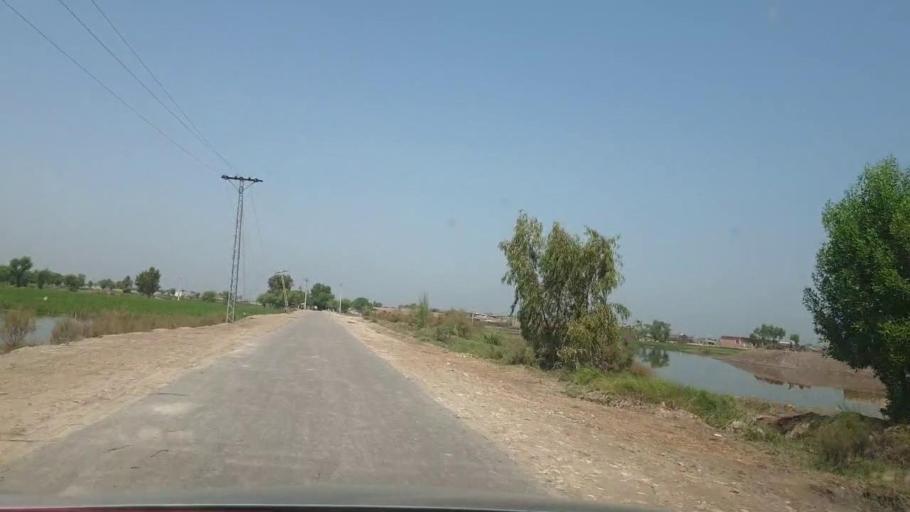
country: PK
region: Sindh
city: Warah
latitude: 27.4775
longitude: 67.7573
